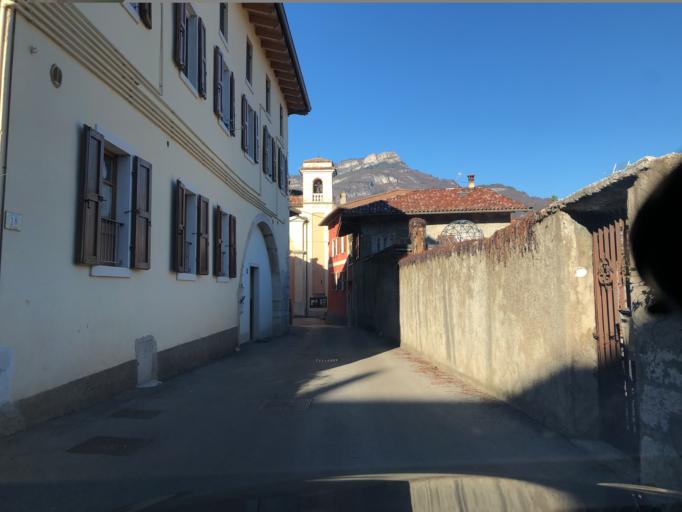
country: IT
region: Trentino-Alto Adige
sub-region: Provincia di Trento
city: Mori
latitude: 45.8380
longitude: 10.9706
